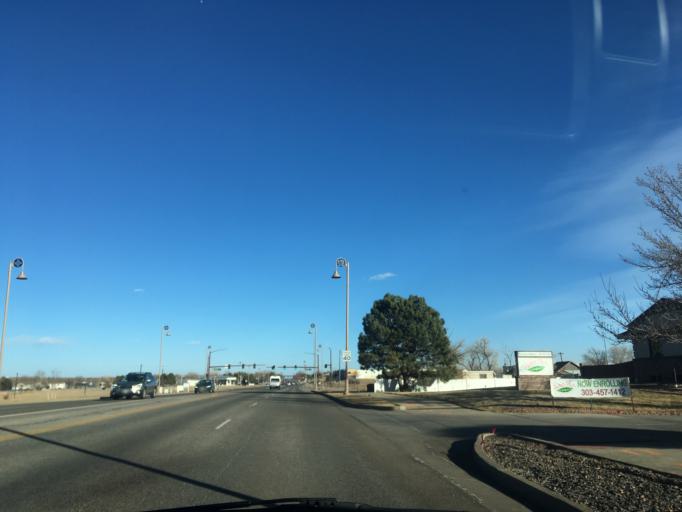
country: US
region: Colorado
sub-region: Adams County
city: Northglenn
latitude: 39.9285
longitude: -104.9837
